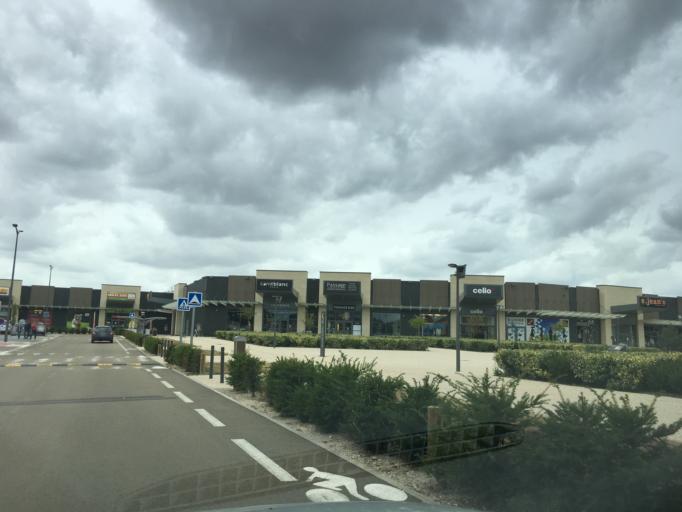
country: FR
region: Bourgogne
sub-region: Departement de l'Yonne
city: Maillot
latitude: 48.1757
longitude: 3.2887
